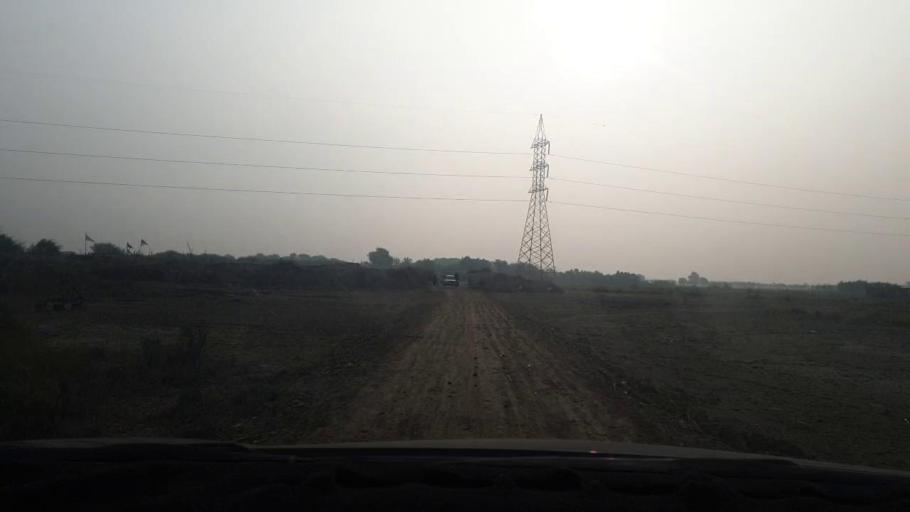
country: PK
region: Sindh
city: Matiari
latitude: 25.5801
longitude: 68.4617
